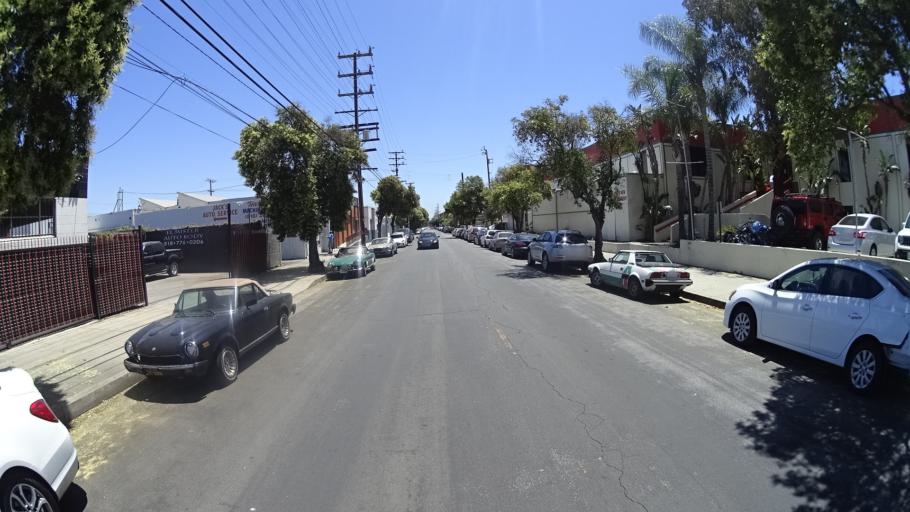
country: US
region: California
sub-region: Los Angeles County
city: Northridge
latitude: 34.1975
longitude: -118.5346
